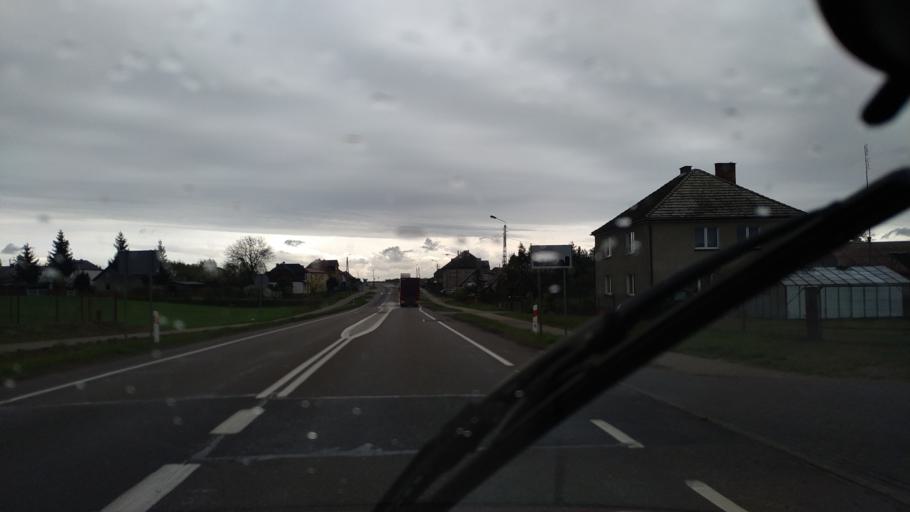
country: PL
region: Pomeranian Voivodeship
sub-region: Powiat starogardzki
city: Kaliska
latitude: 53.8871
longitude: 18.2117
